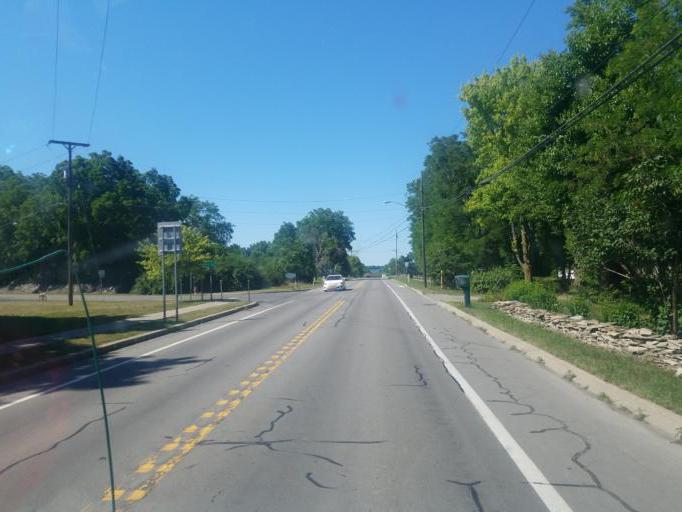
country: US
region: New York
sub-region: Ontario County
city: Phelps
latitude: 42.9654
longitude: -77.0757
